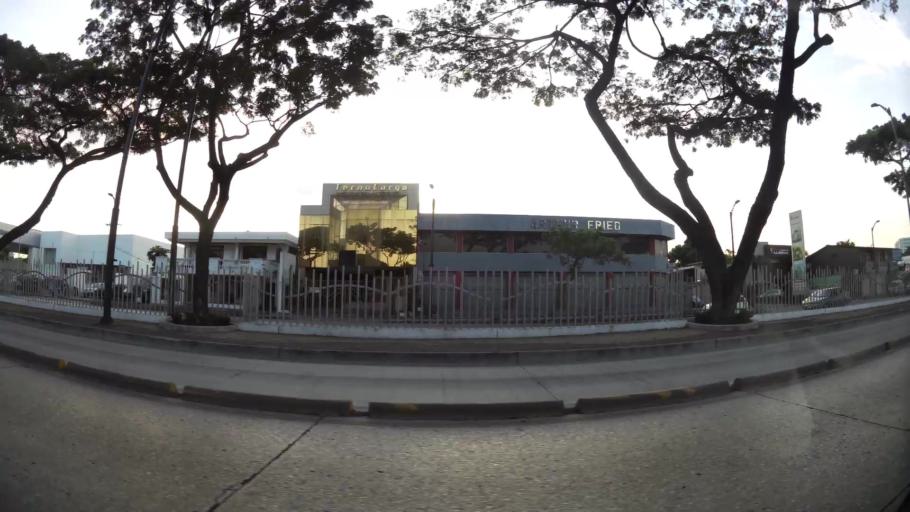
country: EC
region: Guayas
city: Eloy Alfaro
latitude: -2.1613
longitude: -79.8900
